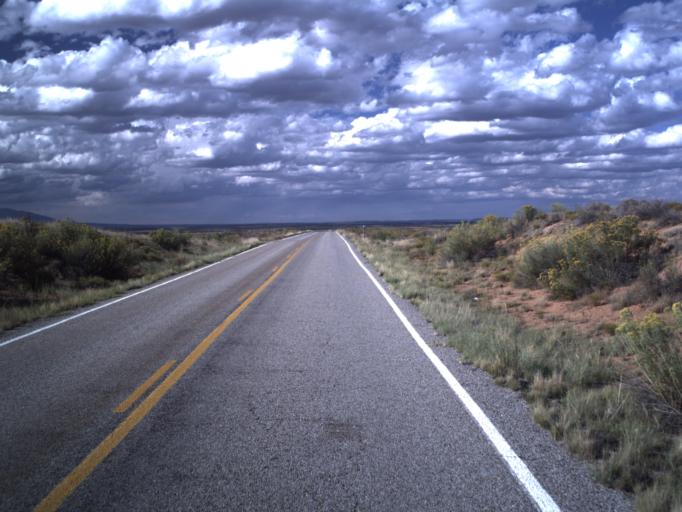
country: US
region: Utah
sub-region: San Juan County
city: Blanding
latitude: 37.3501
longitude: -109.3474
